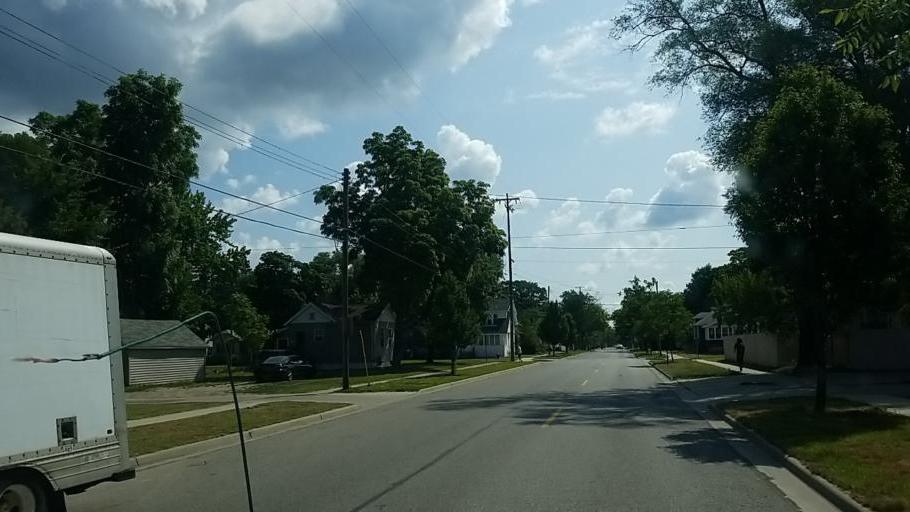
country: US
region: Michigan
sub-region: Muskegon County
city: Muskegon
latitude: 43.2242
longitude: -86.2516
